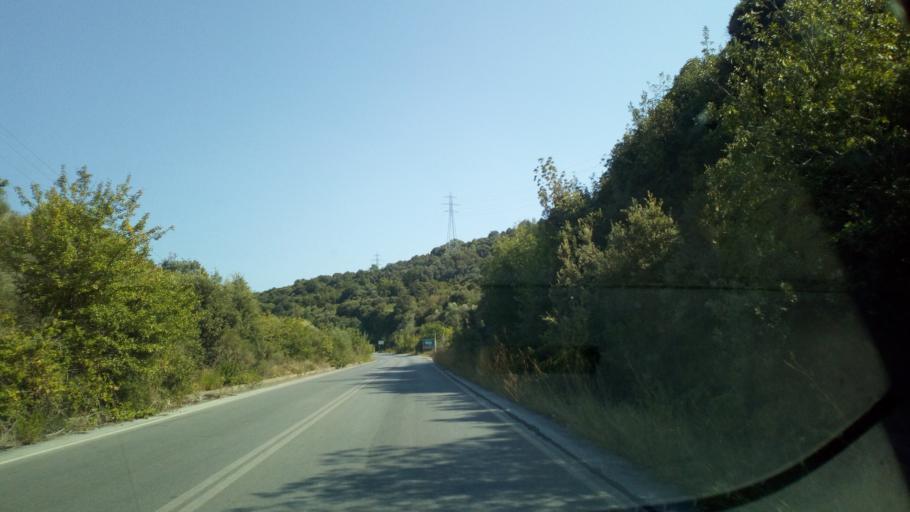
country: GR
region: Central Macedonia
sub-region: Nomos Thessalonikis
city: Stavros
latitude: 40.6352
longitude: 23.7548
